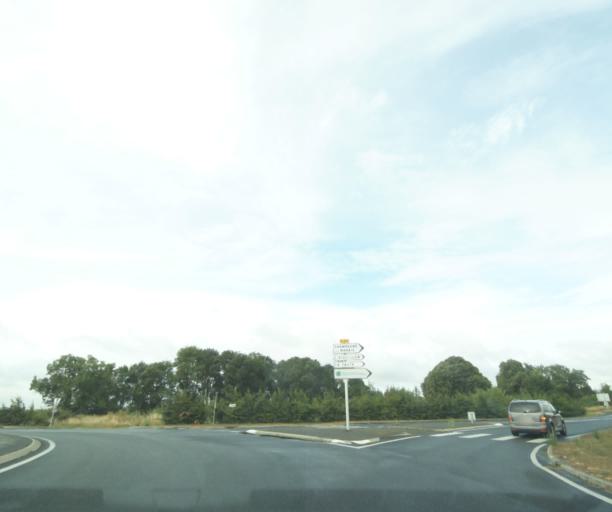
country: FR
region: Pays de la Loire
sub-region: Departement de la Vendee
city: Champagne-les-Marais
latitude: 46.3753
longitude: -1.0923
